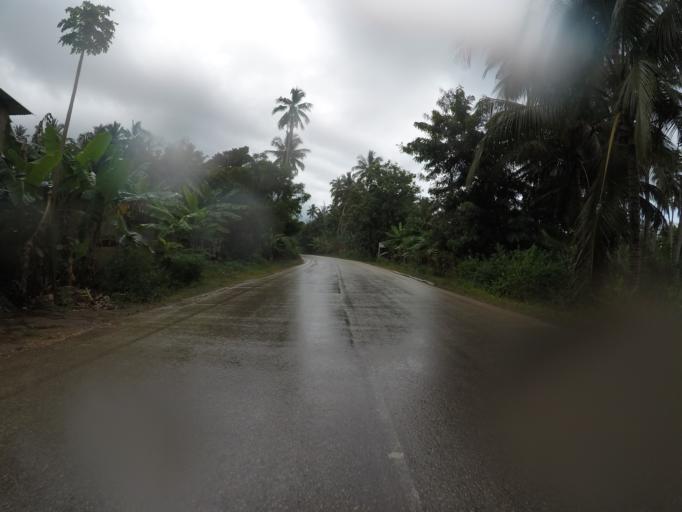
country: TZ
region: Zanzibar North
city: Mkokotoni
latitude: -5.9627
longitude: 39.1948
